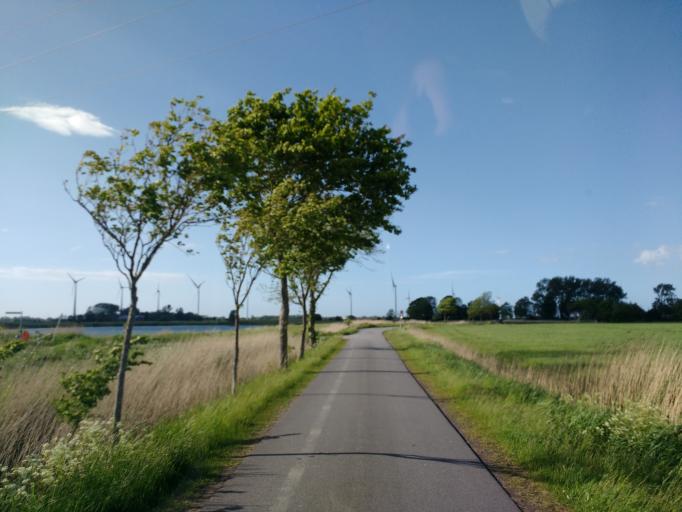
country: DE
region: Lower Saxony
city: Schillig
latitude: 53.6771
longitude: 7.9299
